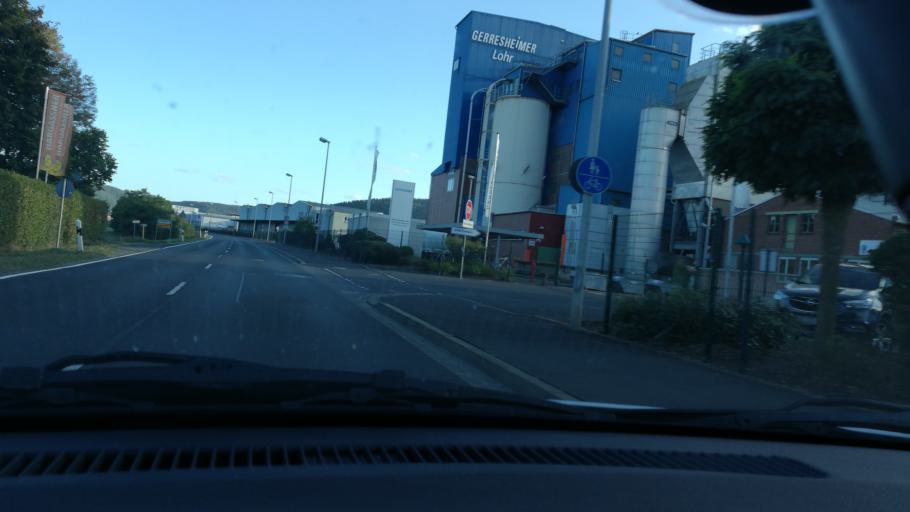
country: DE
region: Bavaria
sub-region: Regierungsbezirk Unterfranken
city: Lohr am Main
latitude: 49.9846
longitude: 9.5795
